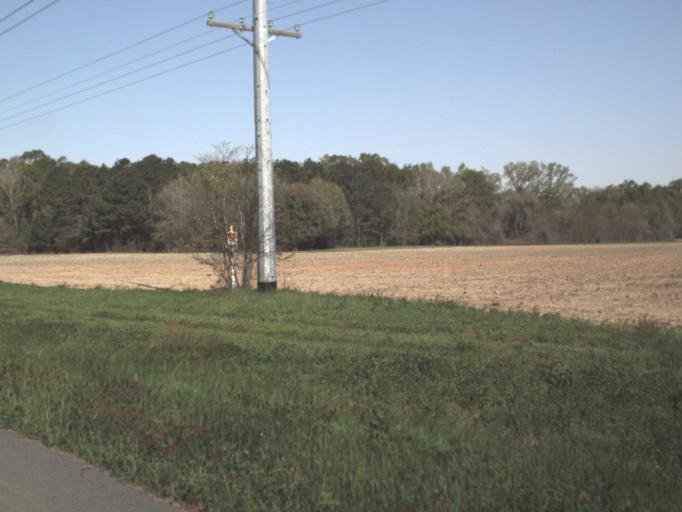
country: US
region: Alabama
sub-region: Houston County
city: Cottonwood
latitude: 30.9358
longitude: -85.3119
